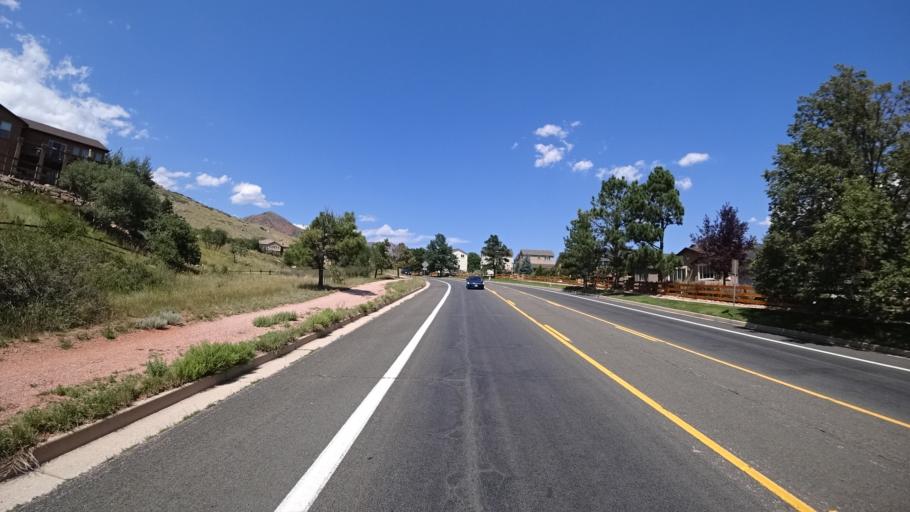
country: US
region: Colorado
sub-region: El Paso County
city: Manitou Springs
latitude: 38.9099
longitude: -104.8744
